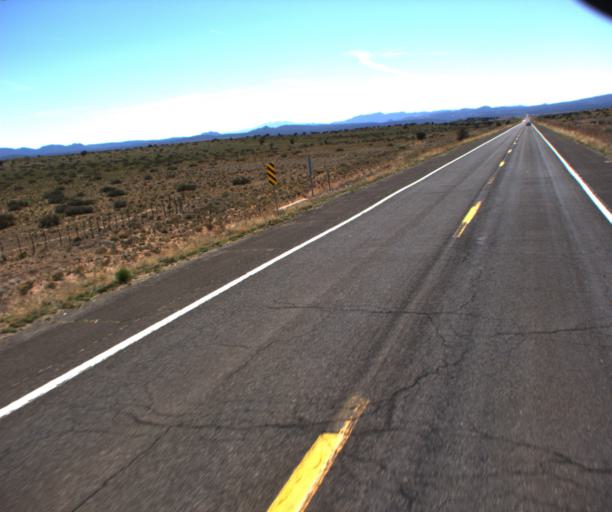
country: US
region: Arizona
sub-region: Mohave County
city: Peach Springs
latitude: 35.5105
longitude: -113.5103
